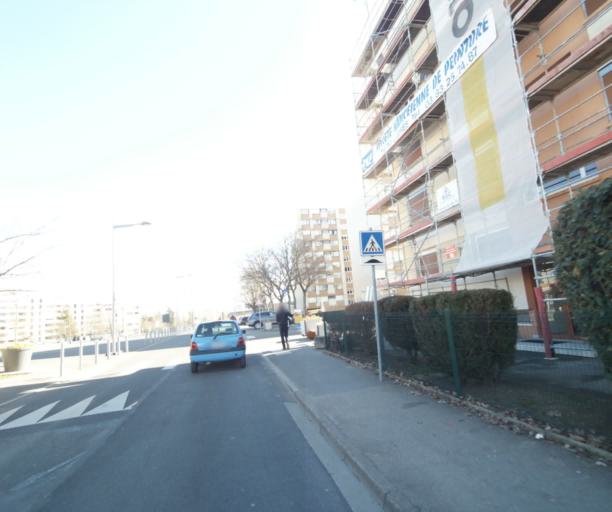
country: FR
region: Lorraine
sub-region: Departement de Meurthe-et-Moselle
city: Vandoeuvre-les-Nancy
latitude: 48.6648
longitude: 6.1728
